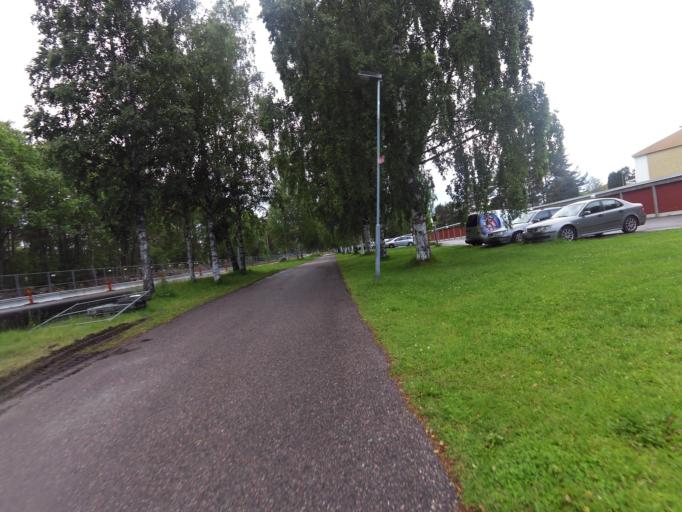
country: SE
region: Gaevleborg
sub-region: Gavle Kommun
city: Gavle
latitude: 60.6922
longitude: 17.1037
